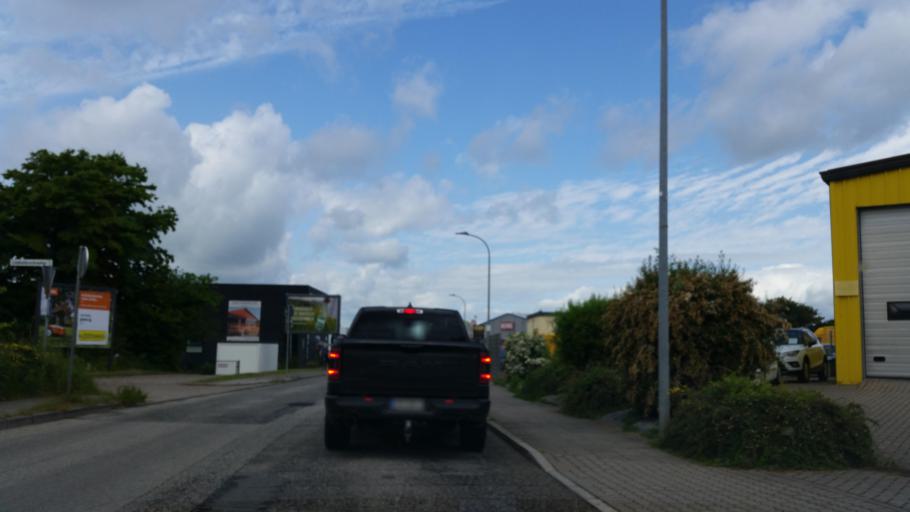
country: DE
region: Schleswig-Holstein
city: Eutin
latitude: 54.1254
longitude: 10.6240
